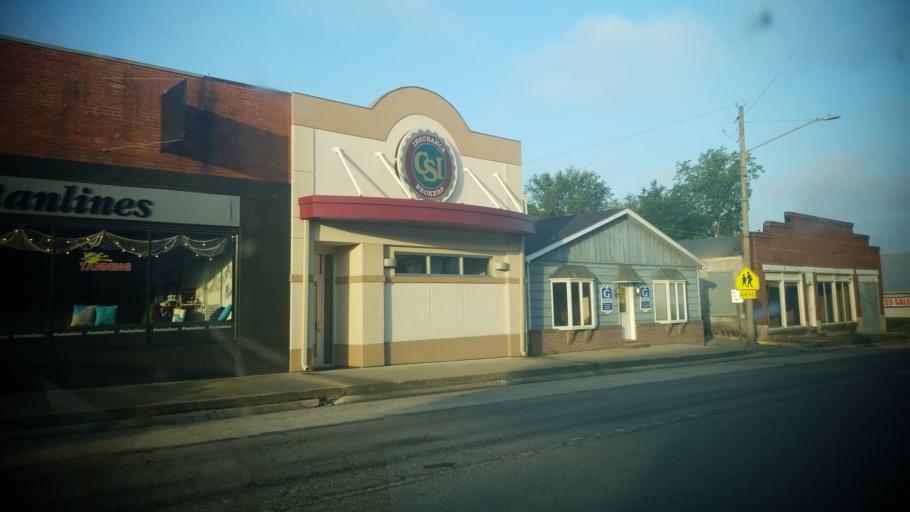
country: US
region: Illinois
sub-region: Wayne County
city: Fairfield
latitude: 38.3797
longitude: -88.3606
